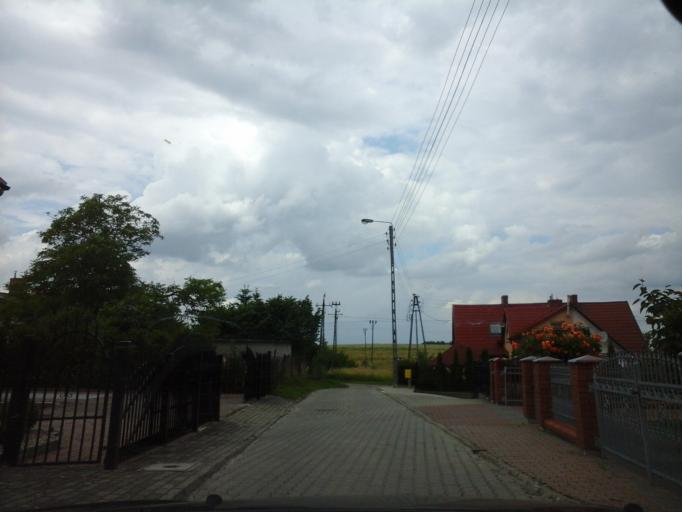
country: PL
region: West Pomeranian Voivodeship
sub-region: Powiat choszczenski
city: Choszczno
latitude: 53.1792
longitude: 15.4111
